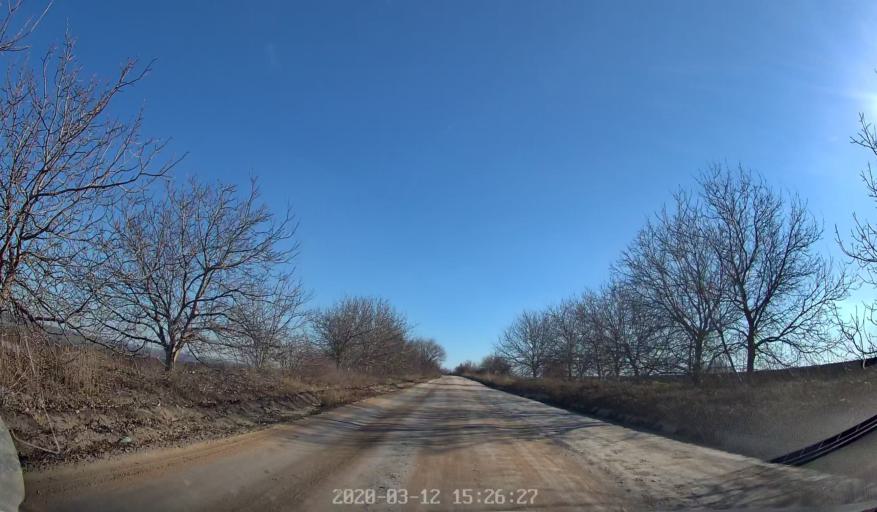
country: MD
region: Chisinau
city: Ciorescu
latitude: 47.1781
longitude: 28.9232
